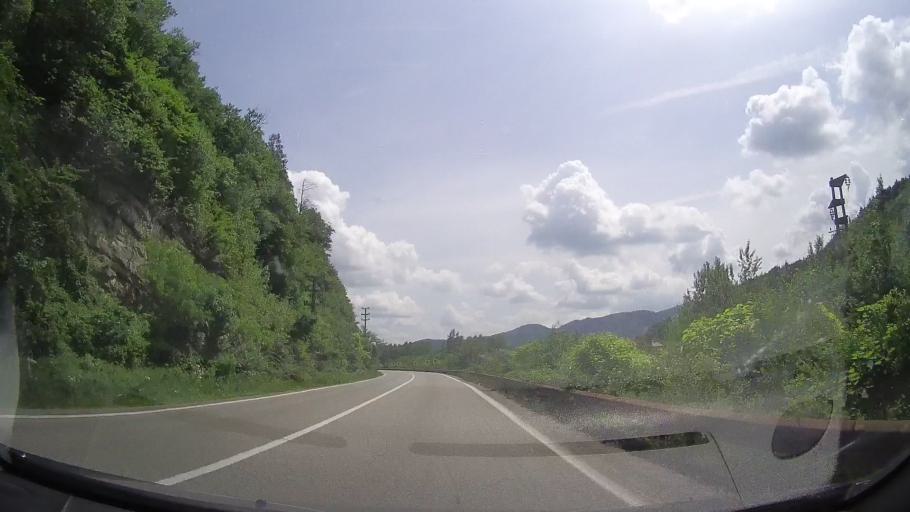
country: RO
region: Valcea
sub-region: Oras Calimanesti
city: Jiblea Veche
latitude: 45.2507
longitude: 24.3400
